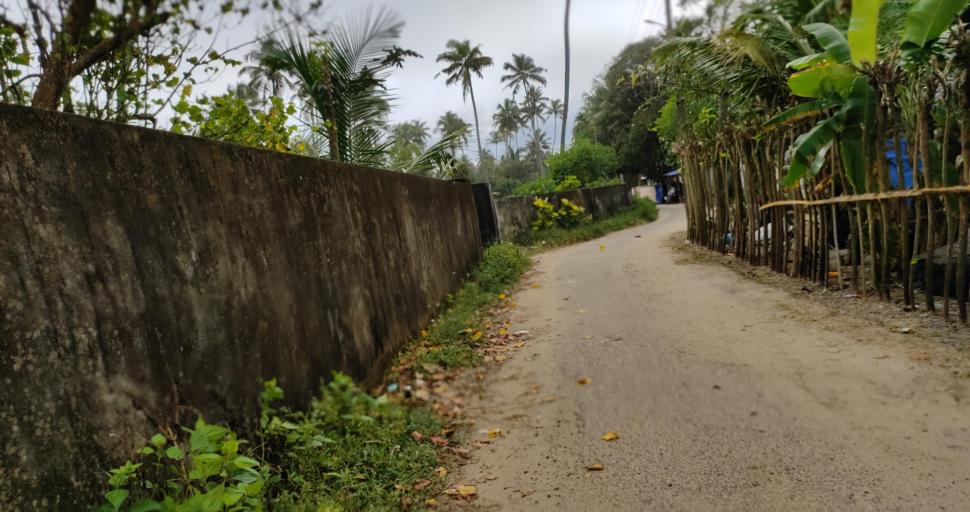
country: IN
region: Kerala
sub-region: Alappuzha
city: Vayalar
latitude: 9.6781
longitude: 76.2911
